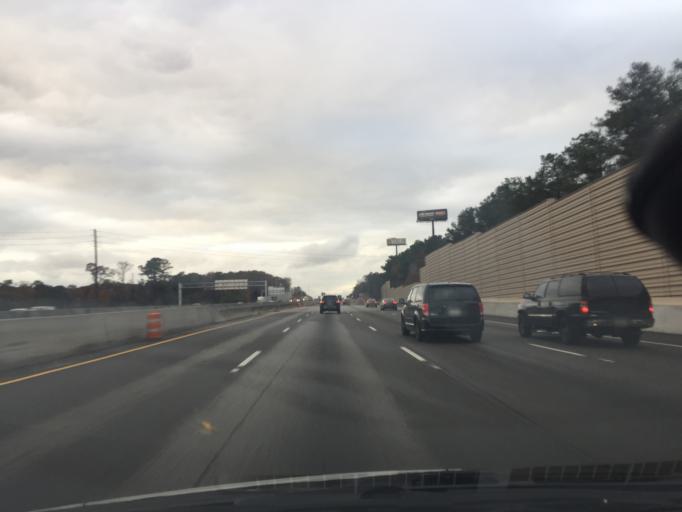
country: US
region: Georgia
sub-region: Henry County
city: Stockbridge
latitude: 33.5170
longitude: -84.2443
